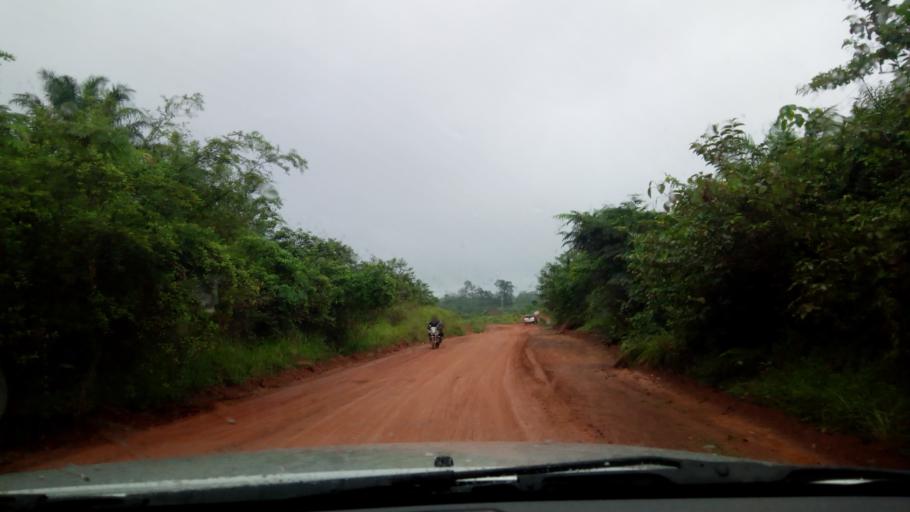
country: LR
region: Nimba
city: Sanniquellie
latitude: 7.1745
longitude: -8.9688
